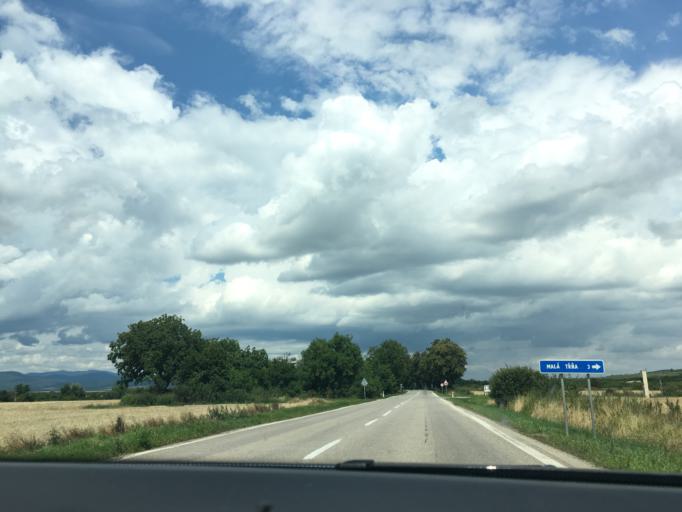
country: HU
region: Borsod-Abauj-Zemplen
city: Satoraljaujhely
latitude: 48.4444
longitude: 21.6535
